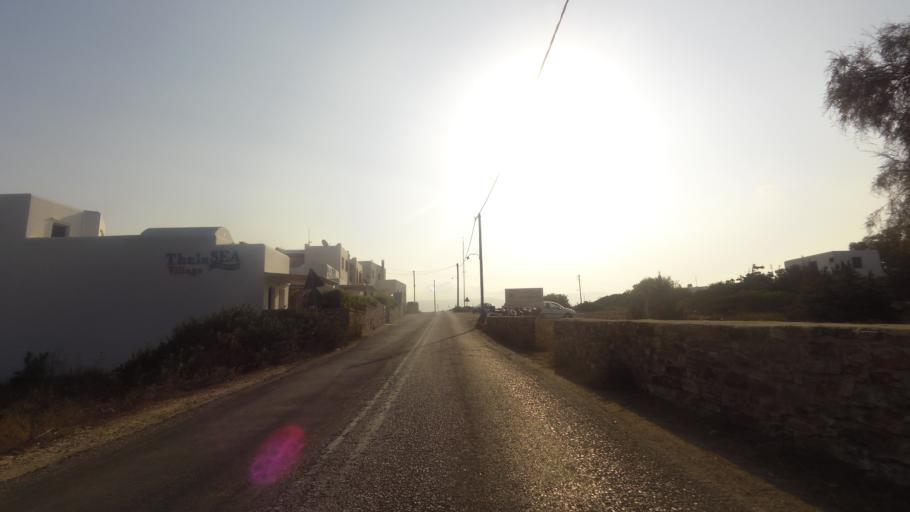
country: GR
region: South Aegean
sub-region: Nomos Kykladon
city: Antiparos
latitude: 37.0375
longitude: 25.0831
